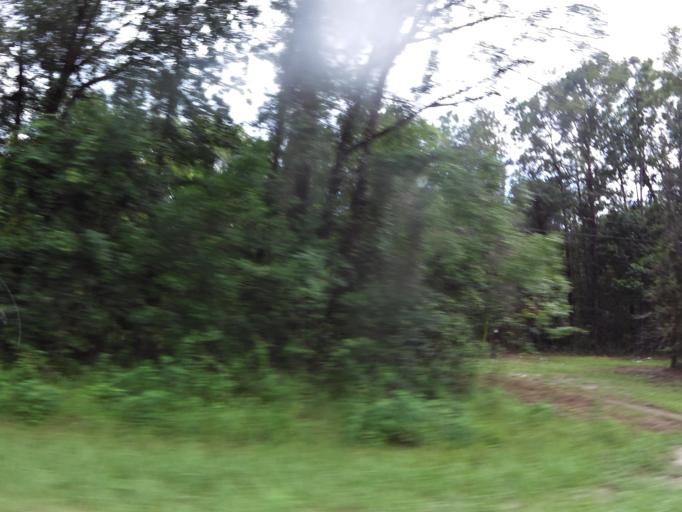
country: US
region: Florida
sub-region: Clay County
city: Asbury Lake
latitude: 30.0761
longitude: -81.7962
